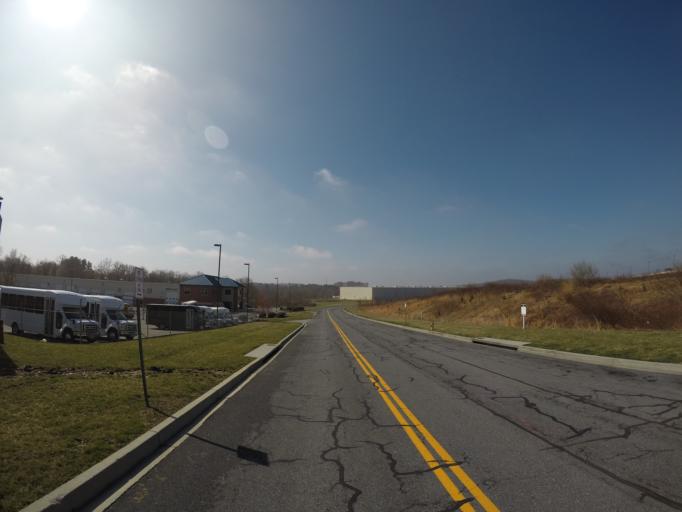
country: US
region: Maryland
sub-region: Frederick County
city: Green Valley
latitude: 39.3760
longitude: -77.2764
